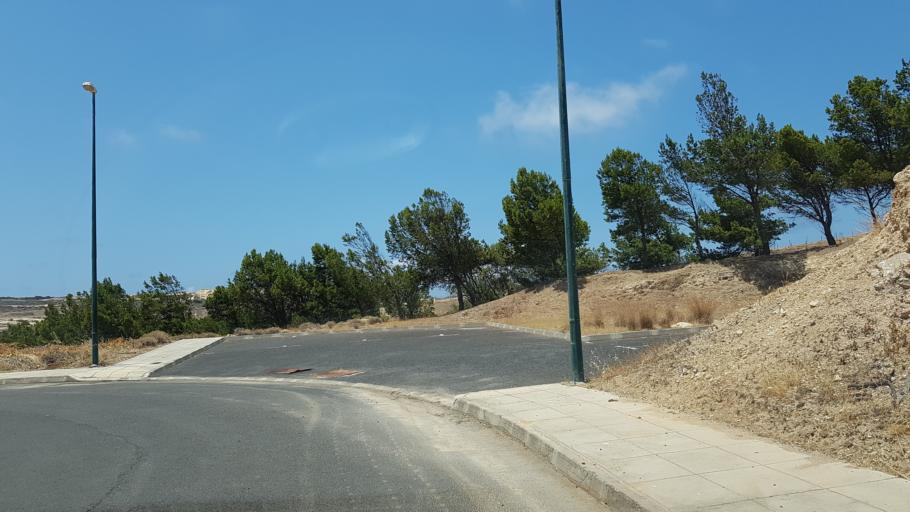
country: PT
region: Madeira
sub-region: Porto Santo
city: Camacha
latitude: 33.0755
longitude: -16.3411
